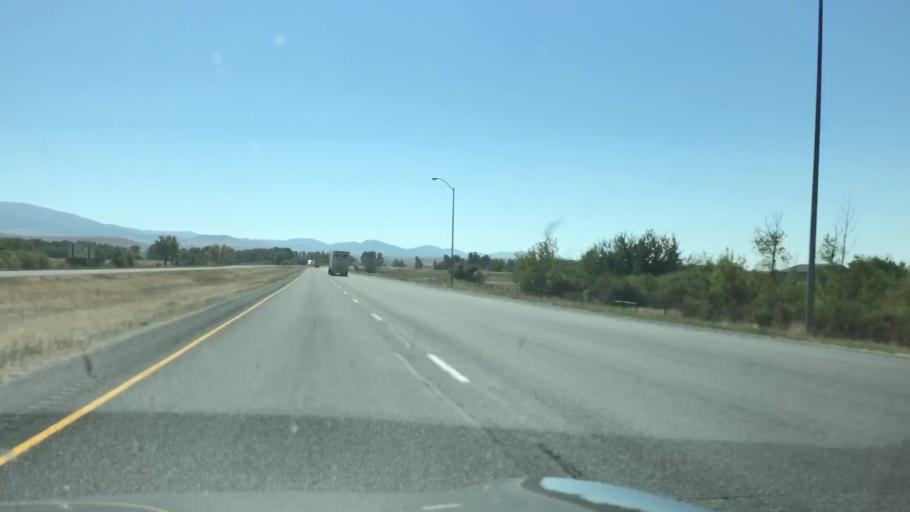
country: US
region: Montana
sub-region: Powell County
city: Deer Lodge
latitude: 46.4078
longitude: -112.7261
